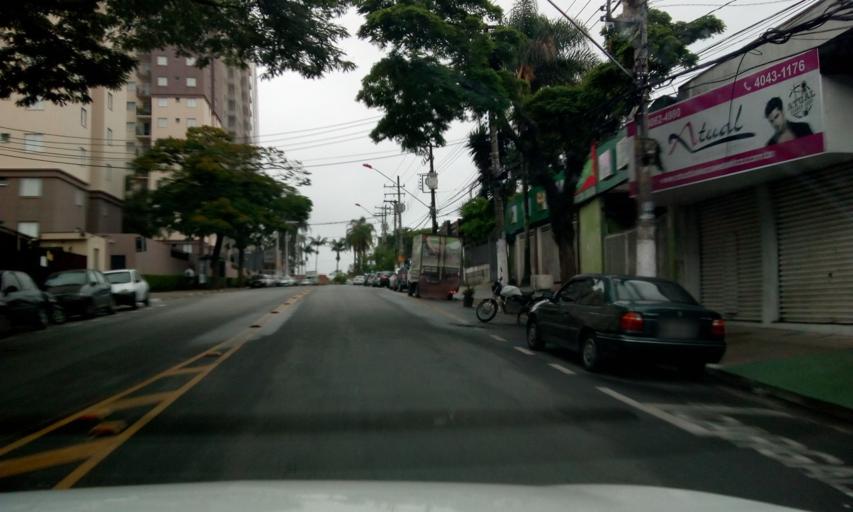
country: BR
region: Sao Paulo
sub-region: Diadema
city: Diadema
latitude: -23.6926
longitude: -46.6202
